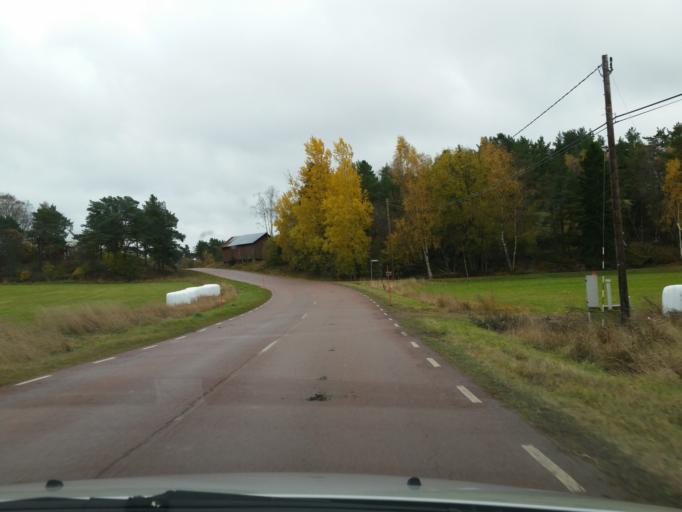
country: AX
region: Alands landsbygd
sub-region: Lumparland
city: Lumparland
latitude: 60.1198
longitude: 20.2497
